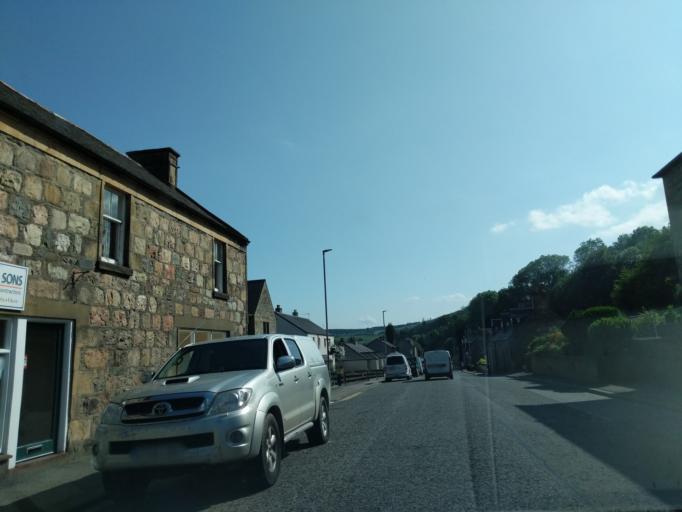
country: GB
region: Scotland
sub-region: Moray
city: Rothes
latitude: 57.5253
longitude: -3.2082
